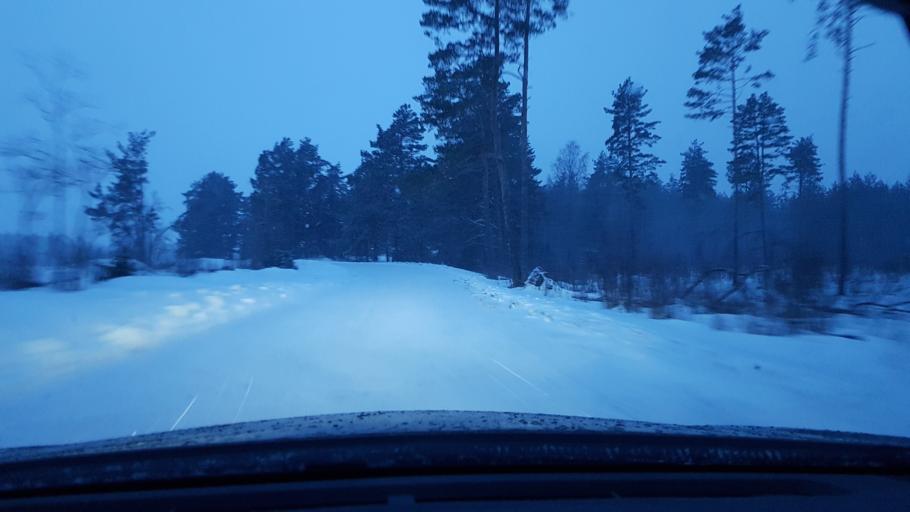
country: EE
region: Harju
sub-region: Kuusalu vald
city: Kuusalu
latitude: 59.4485
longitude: 25.5659
